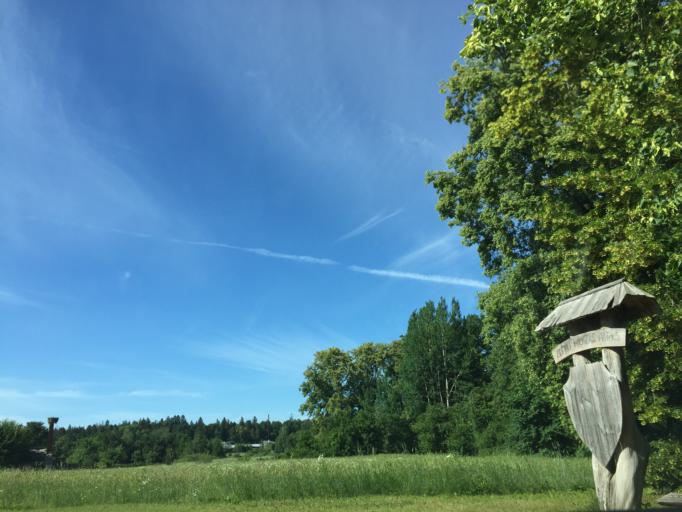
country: LV
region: Ventspils Rajons
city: Piltene
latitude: 57.1158
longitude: 21.8173
